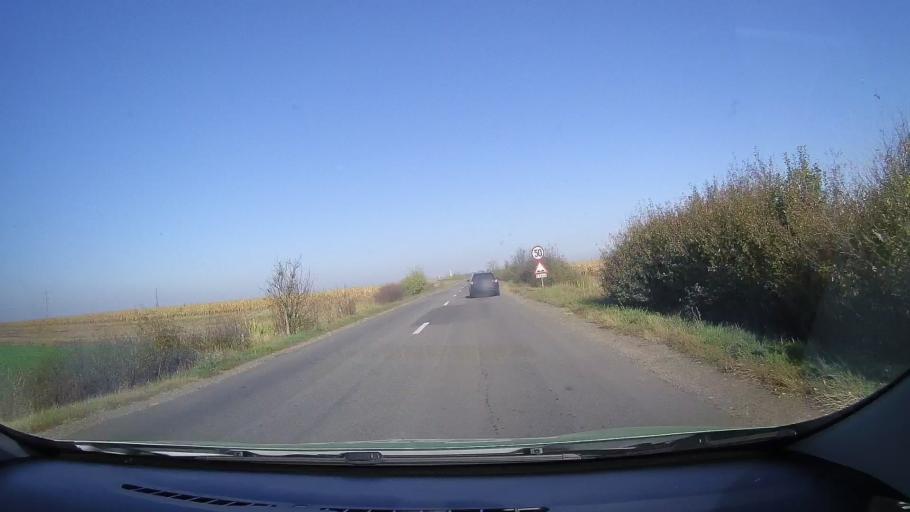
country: RO
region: Satu Mare
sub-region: Comuna Cauas
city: Cauas
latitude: 47.6129
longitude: 22.5380
